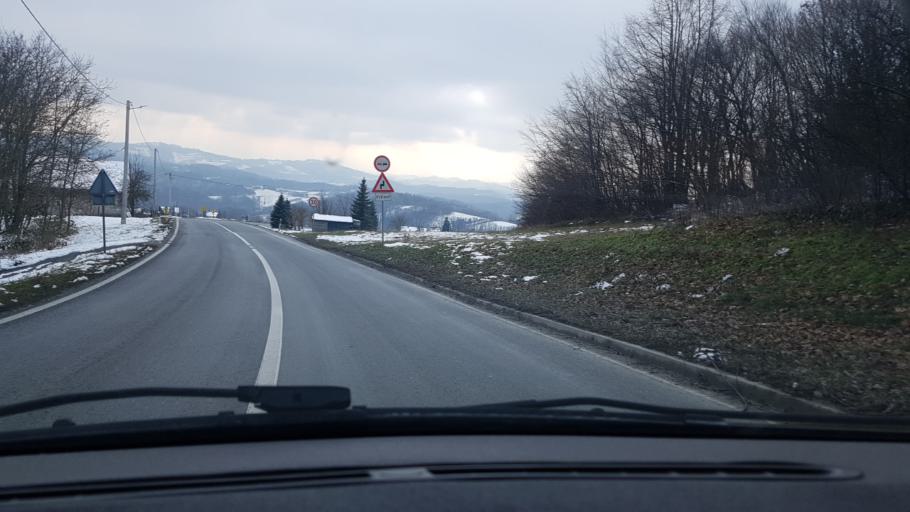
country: HR
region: Krapinsko-Zagorska
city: Mihovljan
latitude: 46.1635
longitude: 15.9633
